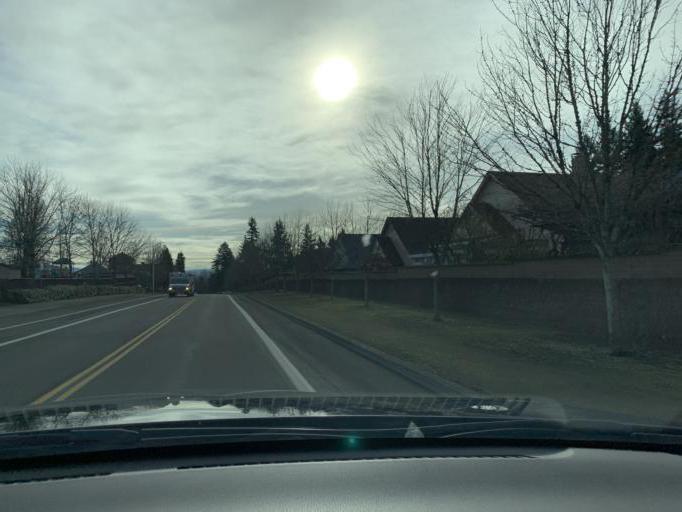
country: US
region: Washington
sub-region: Clark County
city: Mill Plain
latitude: 45.5999
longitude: -122.5059
